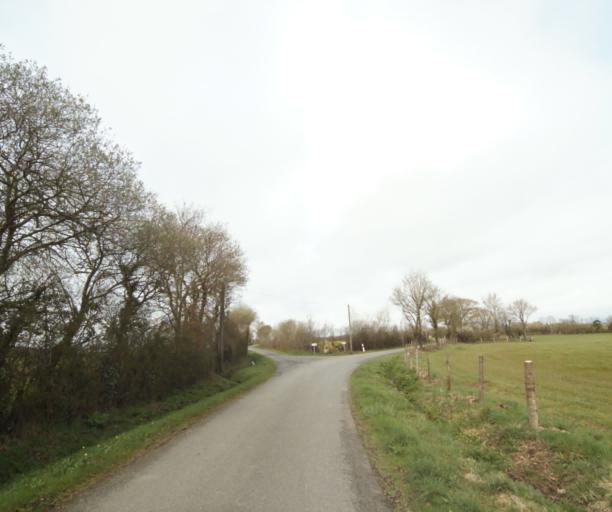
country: FR
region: Pays de la Loire
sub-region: Departement de la Loire-Atlantique
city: Bouvron
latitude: 47.4191
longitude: -1.8769
